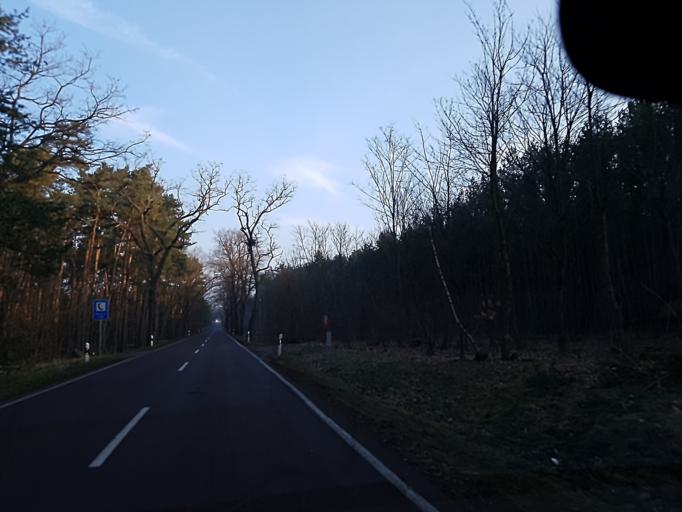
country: DE
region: Saxony-Anhalt
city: Coswig
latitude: 51.9831
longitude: 12.4687
